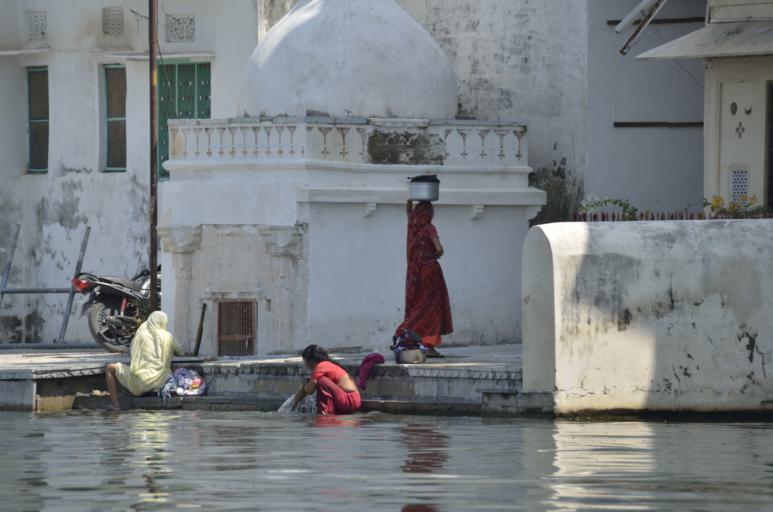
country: IN
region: Rajasthan
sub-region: Udaipur
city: Udaipur
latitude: 24.5780
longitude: 73.6819
